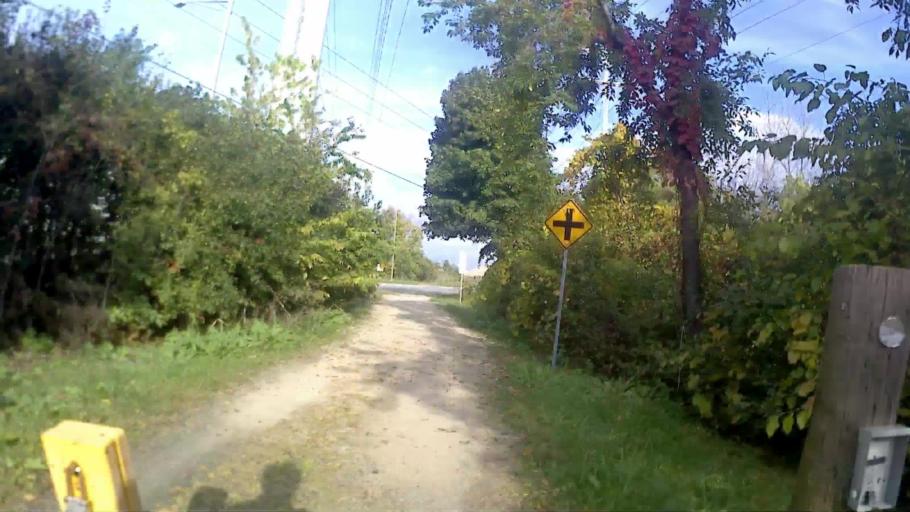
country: US
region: Illinois
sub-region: DuPage County
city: Warrenville
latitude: 41.7987
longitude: -88.2228
